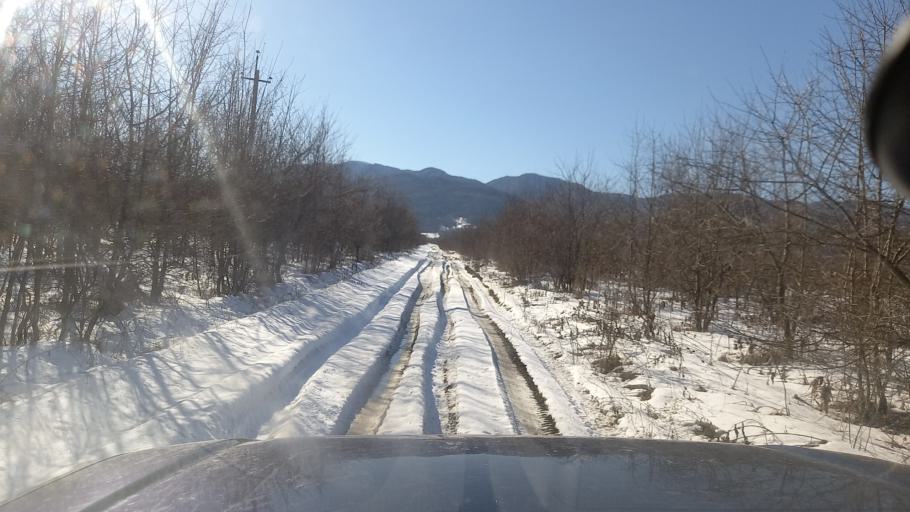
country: RU
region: Adygeya
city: Kamennomostskiy
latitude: 44.2142
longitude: 40.1710
